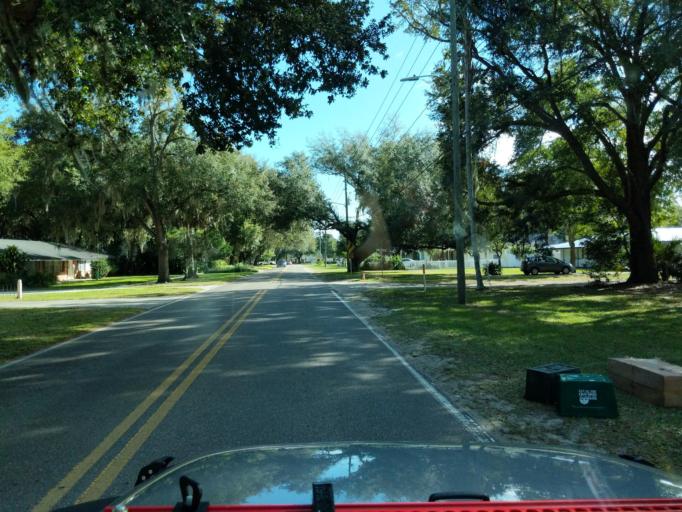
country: US
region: Florida
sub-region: Orange County
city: Oakland
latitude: 28.5552
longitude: -81.6272
